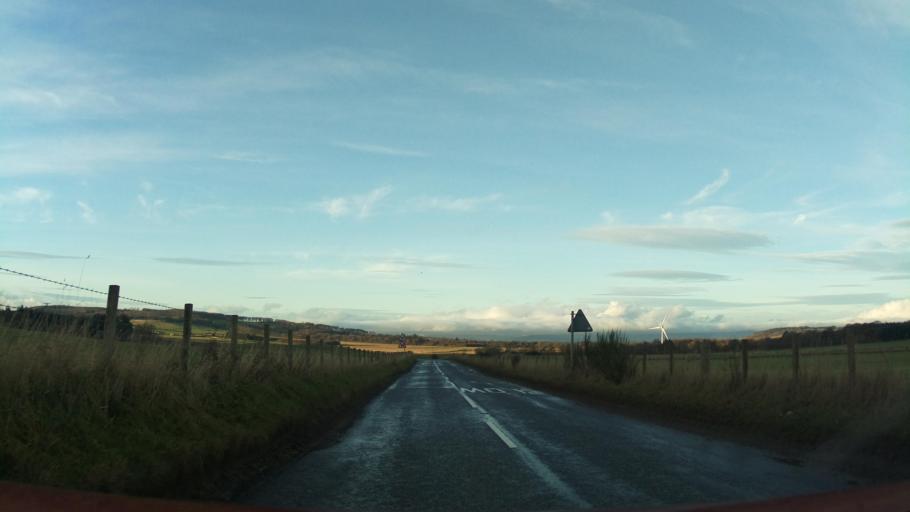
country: GB
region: Scotland
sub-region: Angus
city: Letham
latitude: 56.5827
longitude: -2.8153
